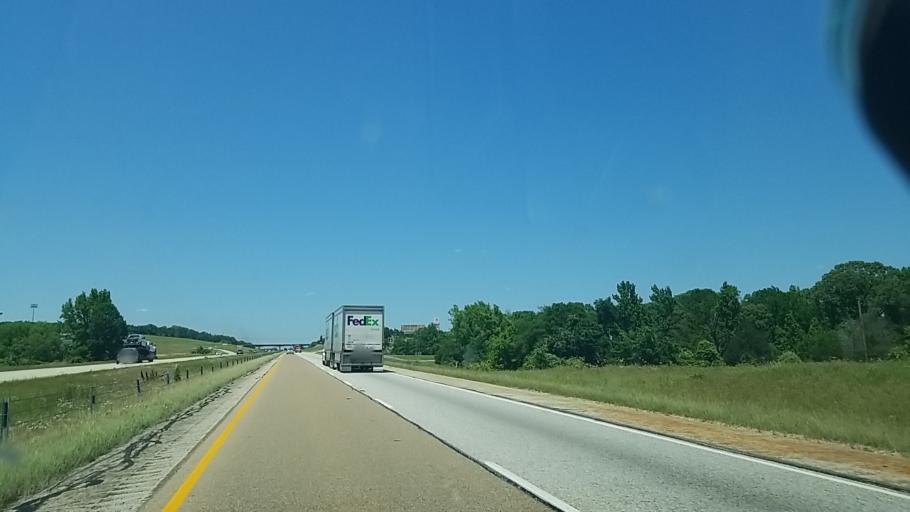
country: US
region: Texas
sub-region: Leon County
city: Centerville
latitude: 31.2515
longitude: -95.9886
